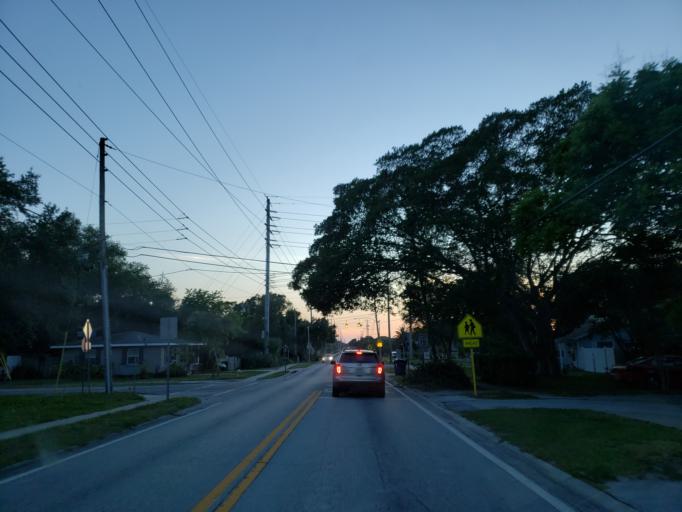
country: US
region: Florida
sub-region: Pinellas County
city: Largo
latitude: 27.9094
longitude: -82.7988
